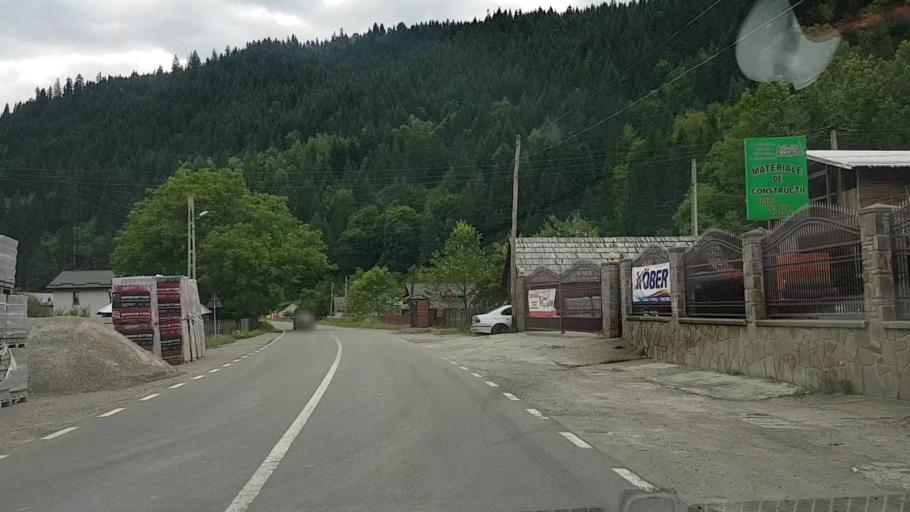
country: RO
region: Neamt
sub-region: Comuna Poiana Teiului
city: Poiana Teiului
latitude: 47.1105
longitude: 25.9318
